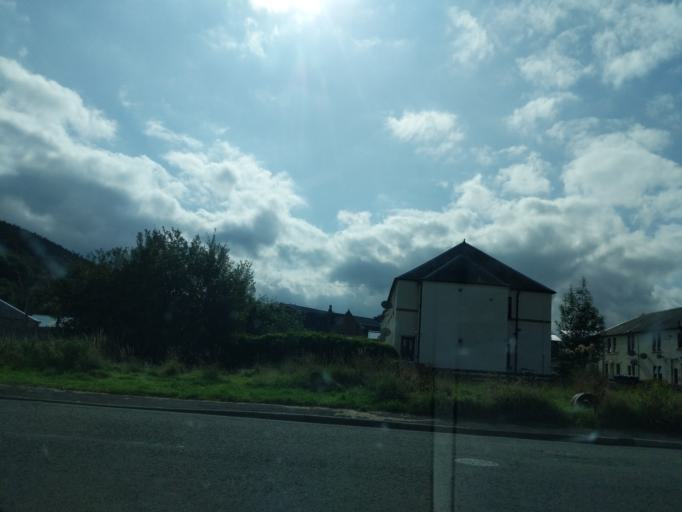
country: GB
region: Scotland
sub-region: The Scottish Borders
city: Peebles
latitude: 55.6582
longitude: -3.1948
